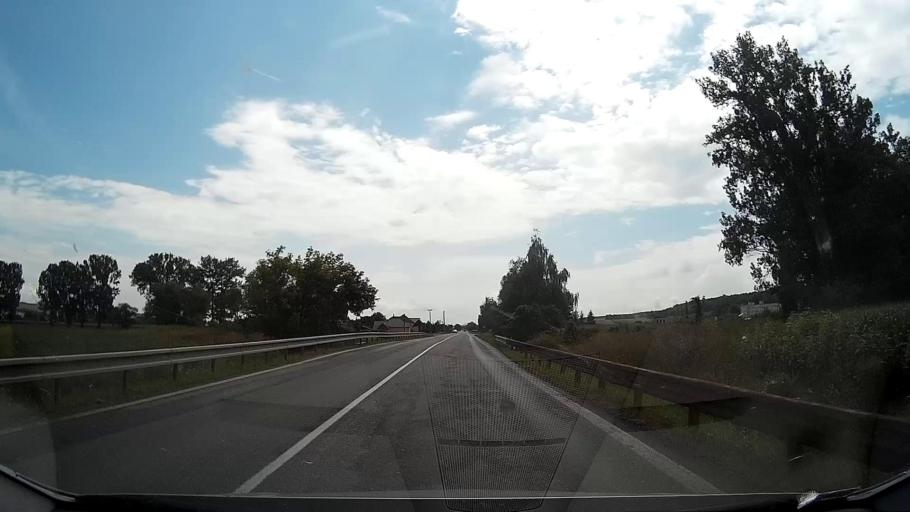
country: SK
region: Banskobystricky
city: Rimavska Sobota
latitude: 48.4091
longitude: 19.9774
